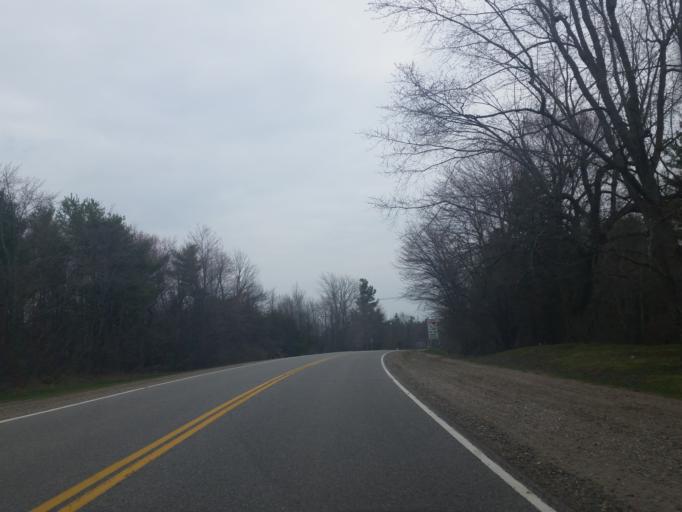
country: US
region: New York
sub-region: Jefferson County
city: Alexandria Bay
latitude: 44.3695
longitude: -75.9899
